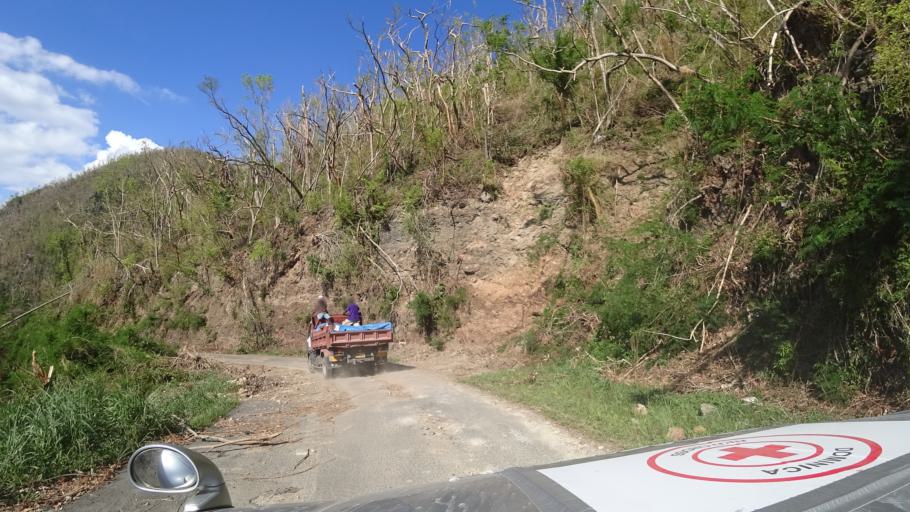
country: DM
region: Saint Luke
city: Pointe Michel
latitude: 15.2445
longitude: -61.3723
